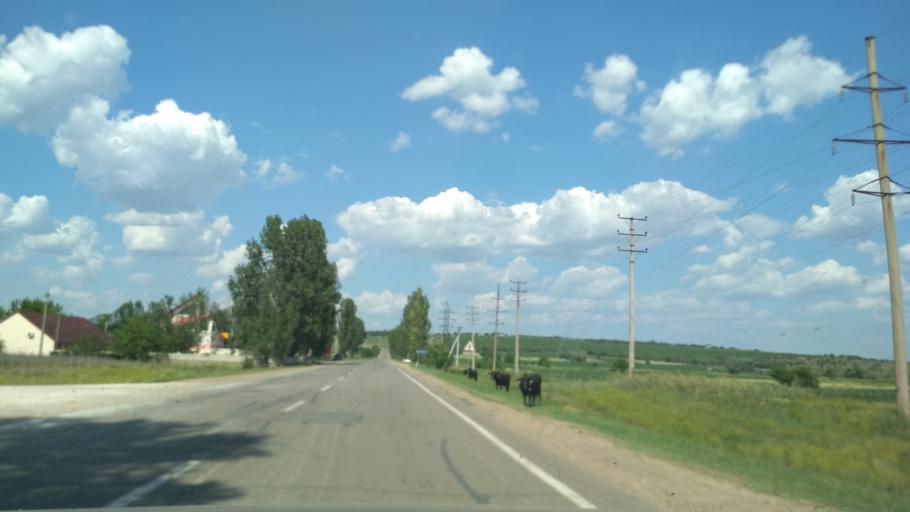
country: MD
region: Criuleni
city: Criuleni
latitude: 47.1510
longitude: 29.1519
